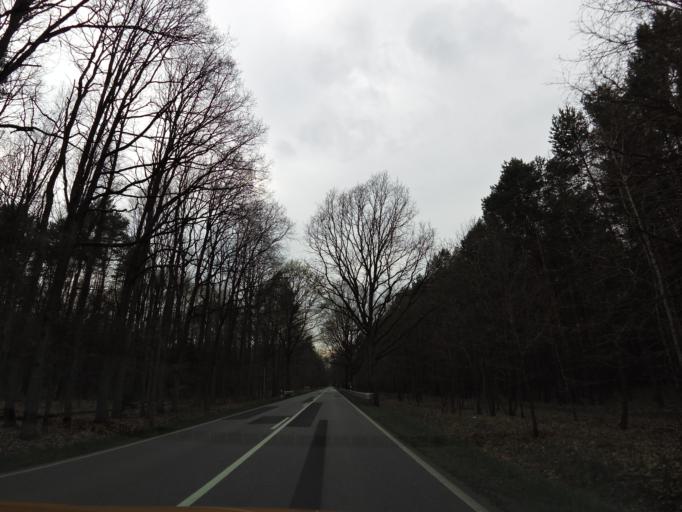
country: DE
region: Brandenburg
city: Mixdorf
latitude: 52.2312
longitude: 14.3719
